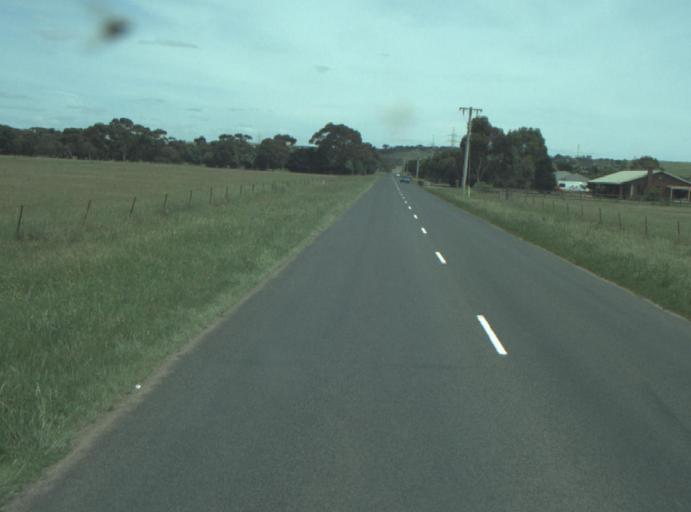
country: AU
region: Victoria
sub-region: Greater Geelong
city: Lara
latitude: -38.0228
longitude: 144.3727
